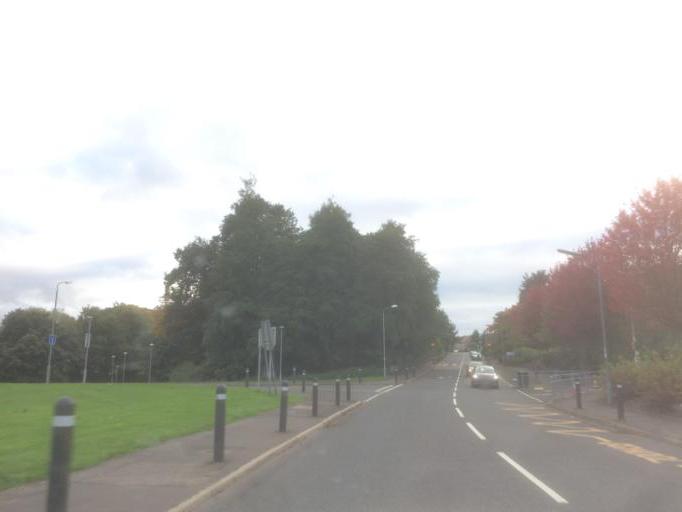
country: GB
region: Scotland
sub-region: East Renfrewshire
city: Giffnock
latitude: 55.8032
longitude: -4.3097
